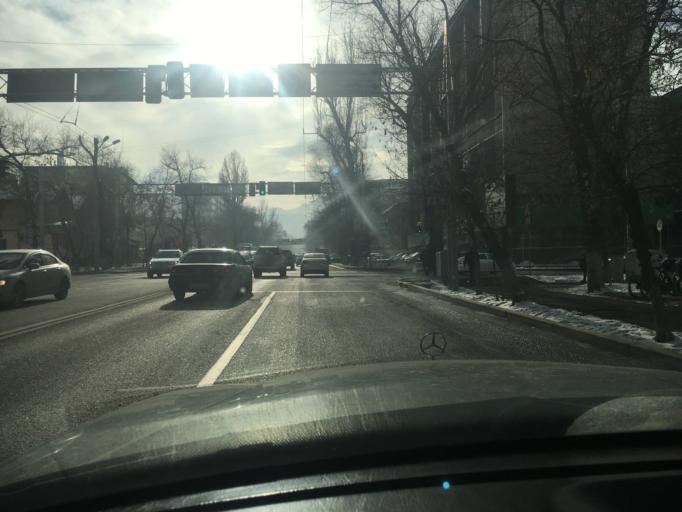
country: KZ
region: Almaty Qalasy
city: Almaty
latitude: 43.2459
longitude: 76.9338
